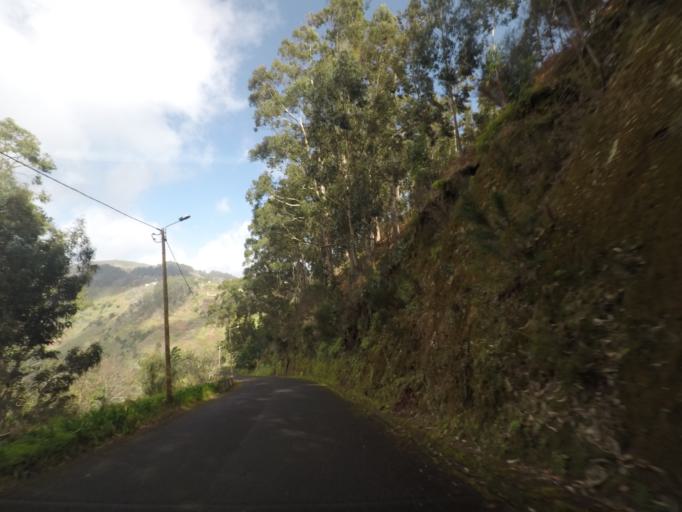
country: PT
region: Madeira
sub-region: Ribeira Brava
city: Campanario
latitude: 32.6982
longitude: -17.0300
